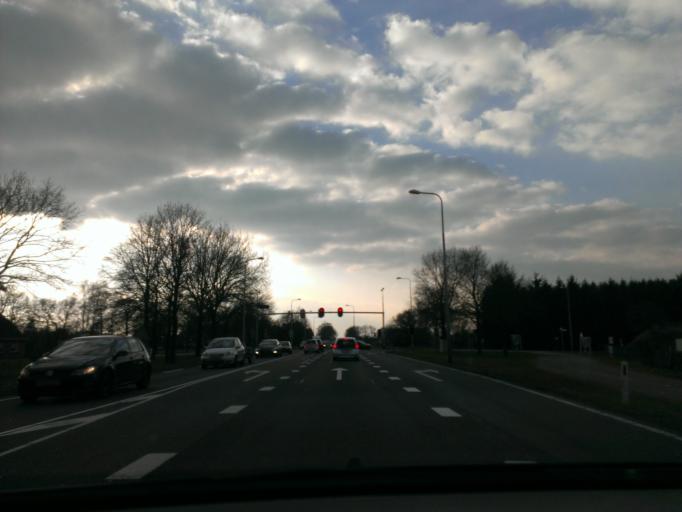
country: NL
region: Overijssel
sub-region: Gemeente Raalte
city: Raalte
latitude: 52.3692
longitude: 6.4005
